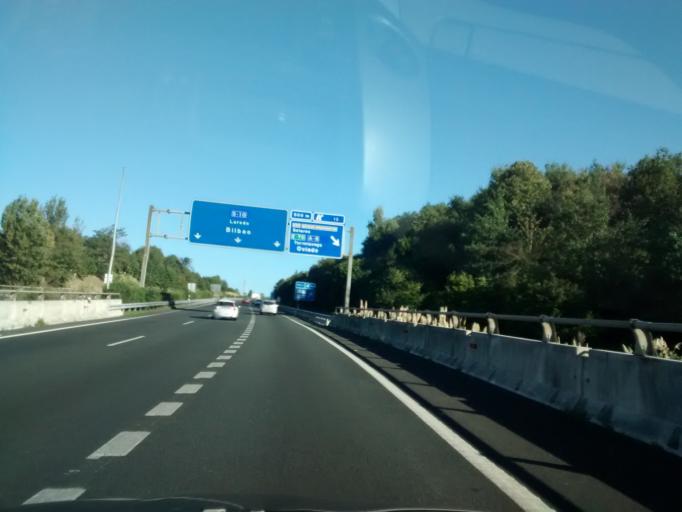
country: ES
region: Cantabria
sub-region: Provincia de Cantabria
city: Lierganes
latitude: 43.3950
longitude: -3.7554
